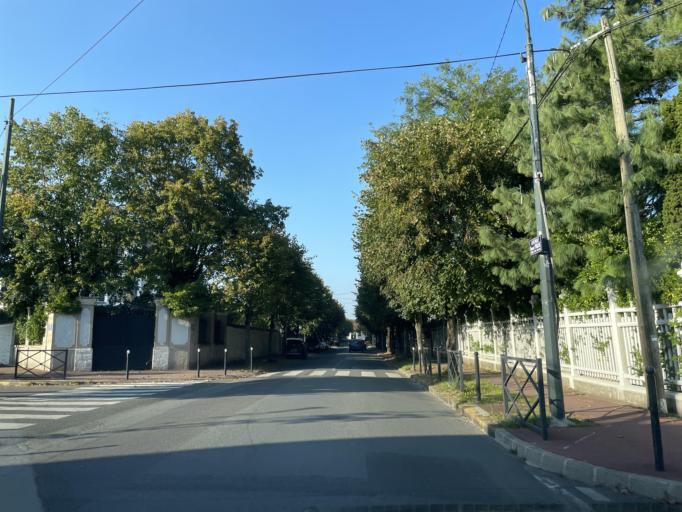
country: FR
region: Ile-de-France
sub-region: Departement du Val-de-Marne
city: Chennevieres-sur-Marne
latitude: 48.8036
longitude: 2.5180
